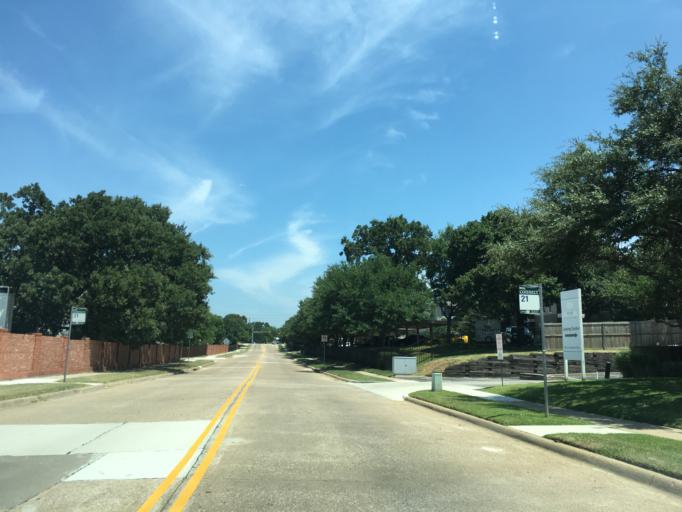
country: US
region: Texas
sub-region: Denton County
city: Lewisville
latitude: 33.0246
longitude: -96.9994
